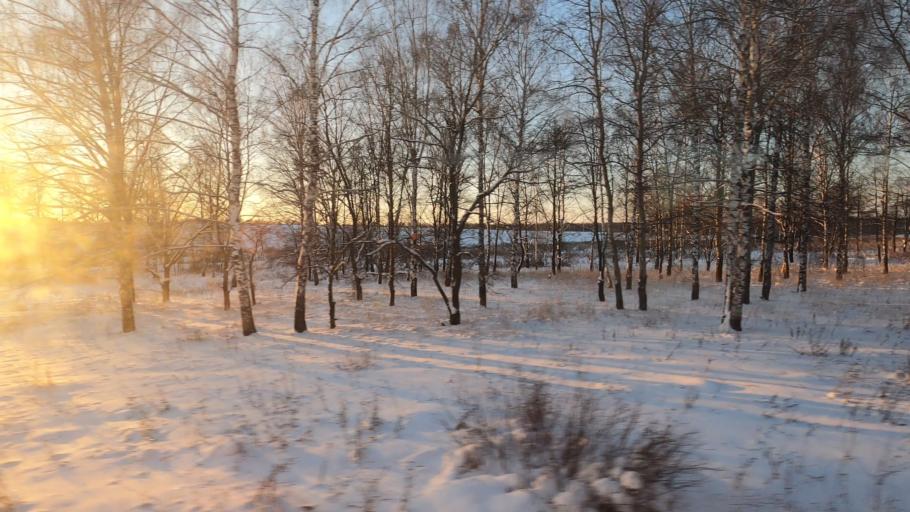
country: RU
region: Moskovskaya
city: Orud'yevo
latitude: 56.4111
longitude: 37.4963
